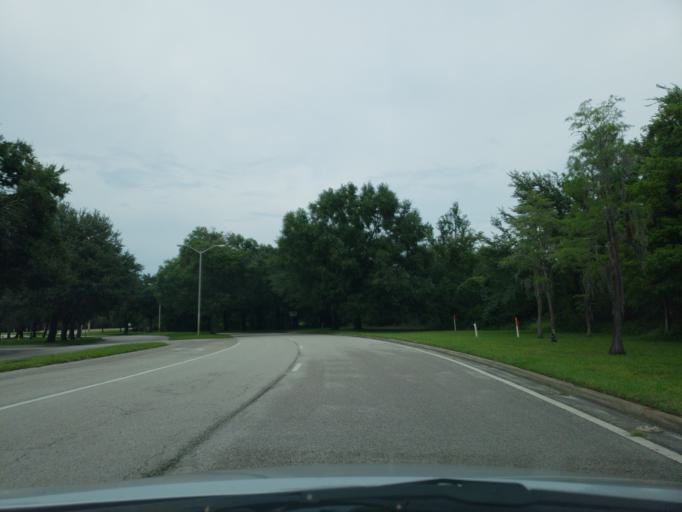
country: US
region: Florida
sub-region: Hillsborough County
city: Temple Terrace
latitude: 28.0673
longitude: -82.3702
